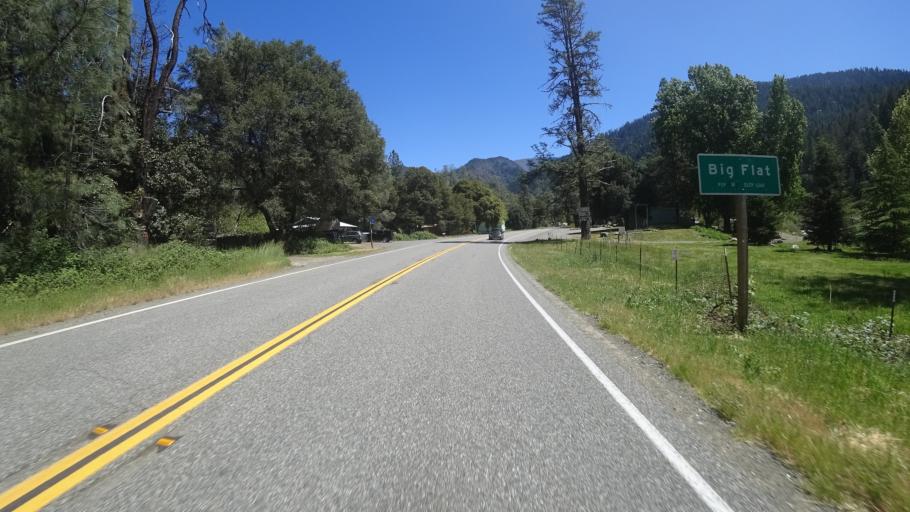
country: US
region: California
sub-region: Trinity County
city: Hayfork
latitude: 40.7418
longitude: -123.2121
